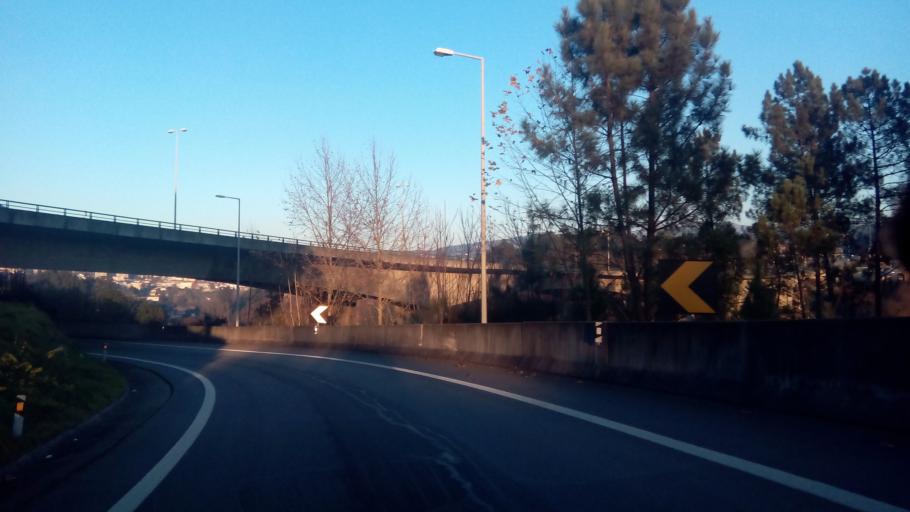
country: PT
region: Porto
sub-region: Amarante
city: Amarante
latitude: 41.2584
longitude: -8.0952
